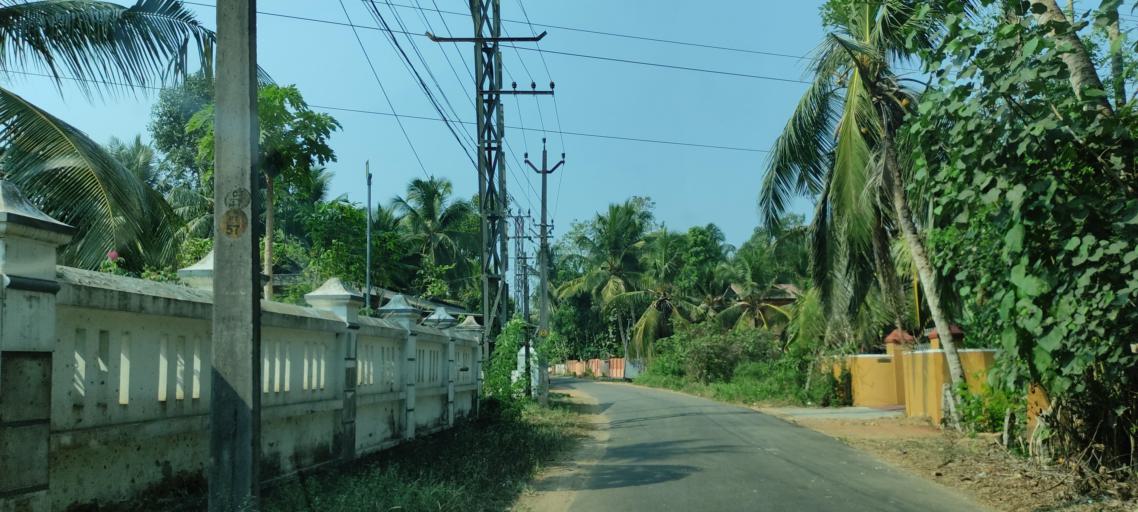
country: IN
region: Kerala
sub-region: Pattanamtitta
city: Tiruvalla
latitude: 9.3571
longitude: 76.5152
